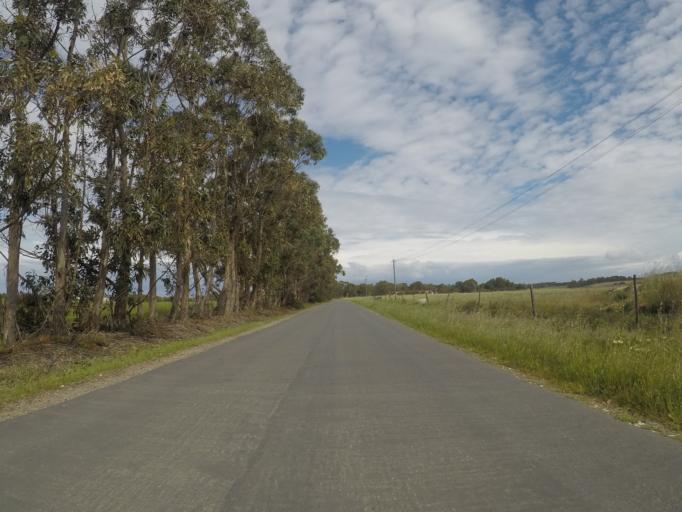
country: PT
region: Beja
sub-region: Odemira
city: Sao Teotonio
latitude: 37.4927
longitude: -8.7831
